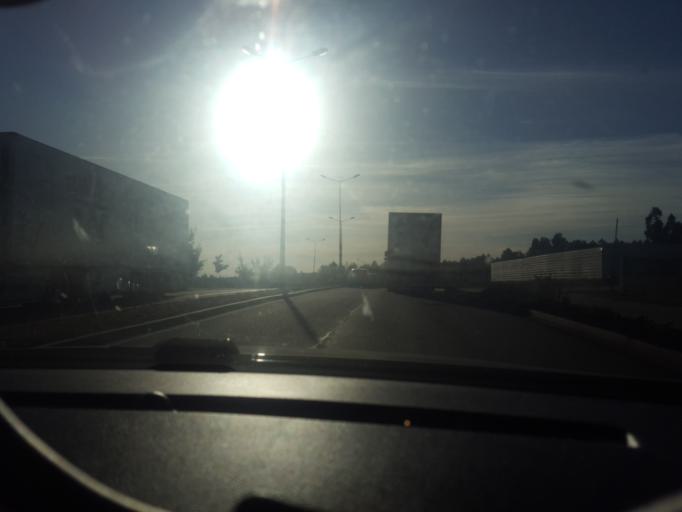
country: PT
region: Viseu
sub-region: Nelas
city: Nelas
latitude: 40.5423
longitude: -7.8469
